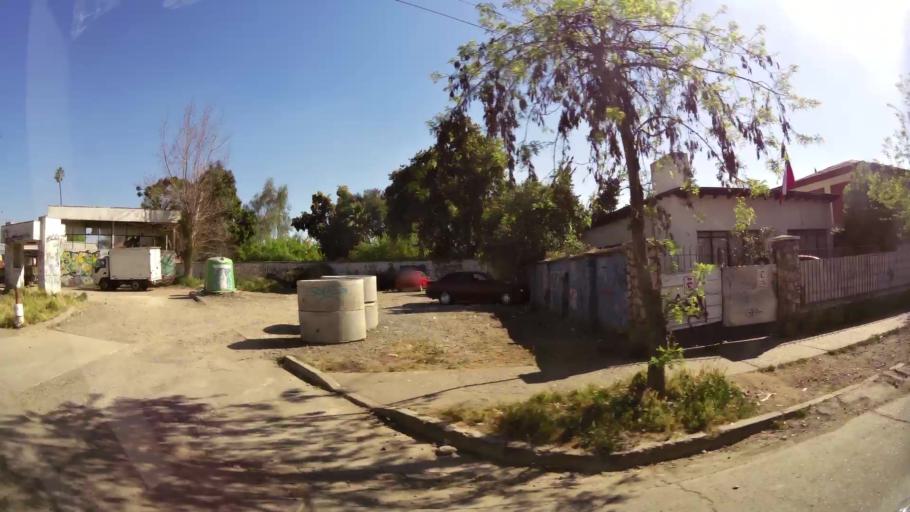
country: CL
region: Santiago Metropolitan
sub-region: Provincia de Talagante
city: Penaflor
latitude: -33.6068
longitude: -70.8986
